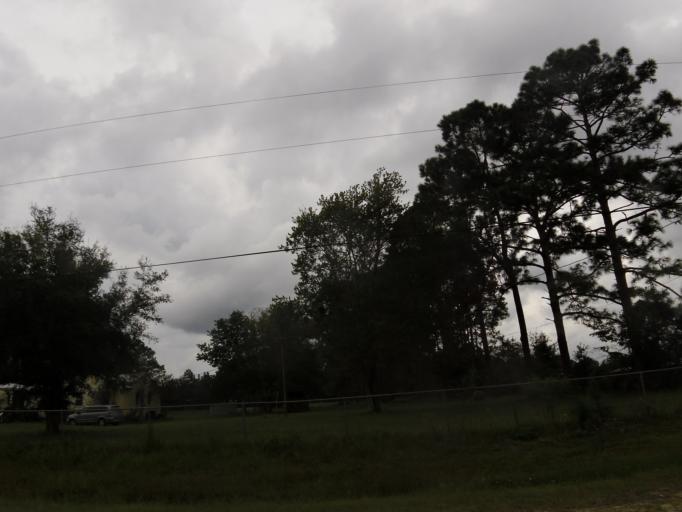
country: US
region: Florida
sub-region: Clay County
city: Middleburg
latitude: 30.1230
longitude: -81.9493
